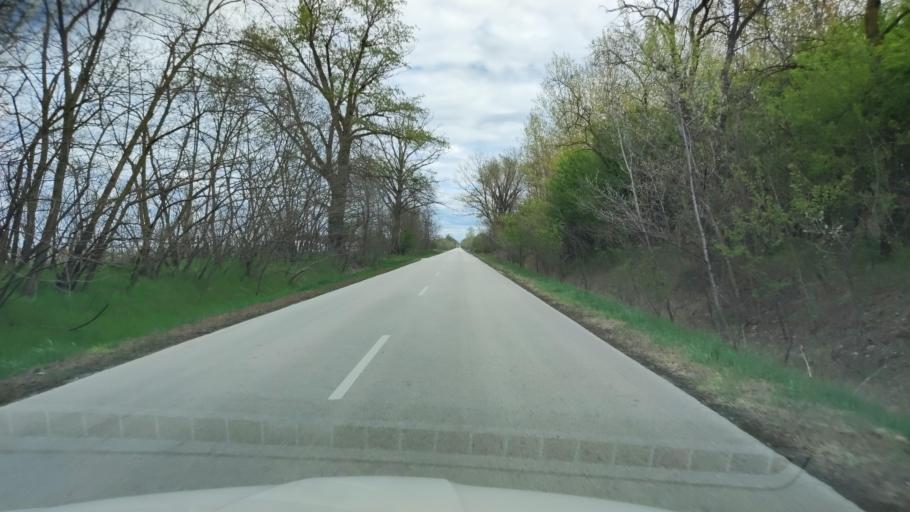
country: HU
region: Pest
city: Kocser
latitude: 47.0545
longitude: 19.9542
